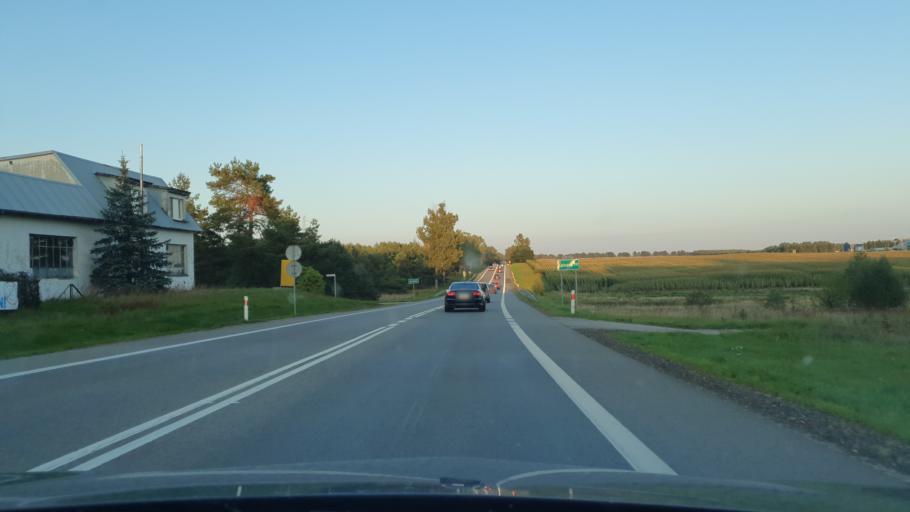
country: PL
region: Pomeranian Voivodeship
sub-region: Powiat slupski
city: Potegowo
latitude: 54.4764
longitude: 17.4928
